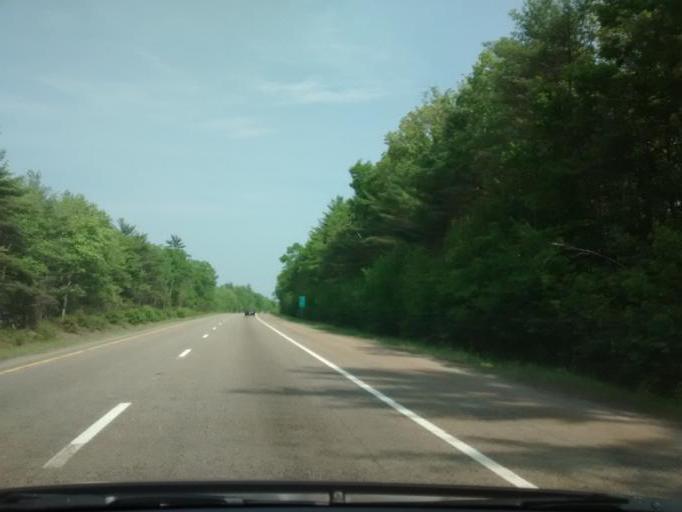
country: US
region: Massachusetts
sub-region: Plymouth County
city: Carver
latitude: 41.8440
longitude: -70.8396
